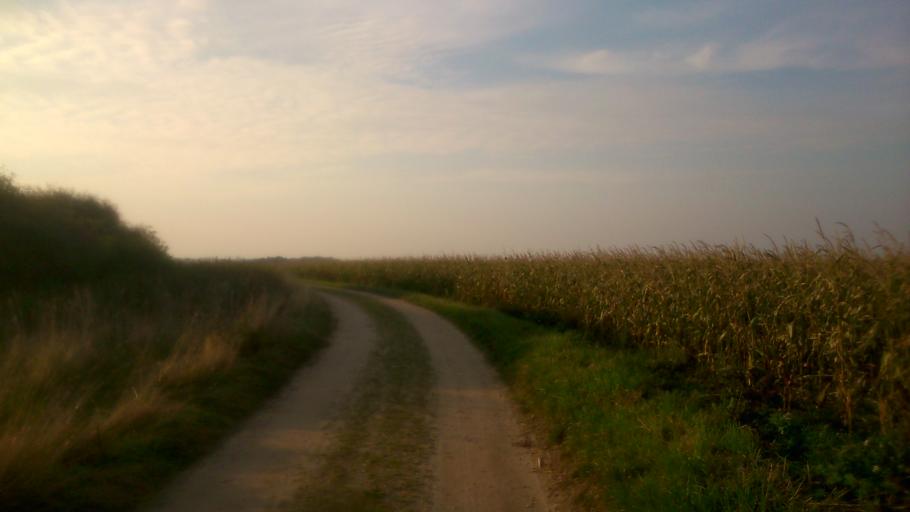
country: DK
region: Central Jutland
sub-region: Ringkobing-Skjern Kommune
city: Ringkobing
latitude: 56.1078
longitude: 8.1640
